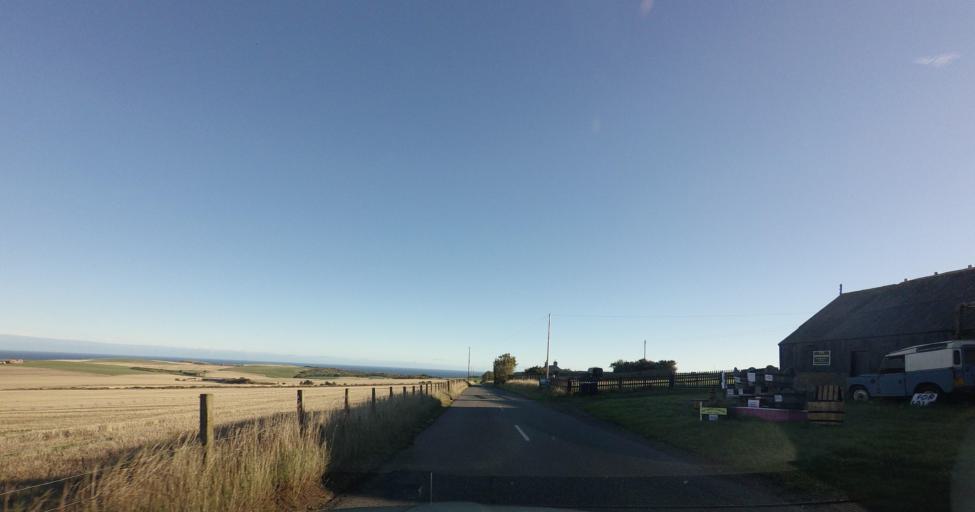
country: GB
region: Scotland
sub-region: Aberdeenshire
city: Macduff
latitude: 57.6663
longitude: -2.3113
